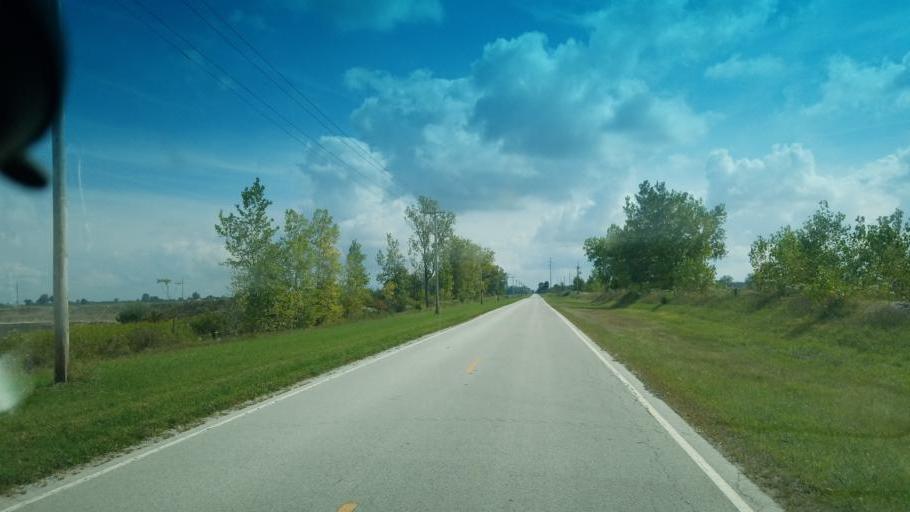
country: US
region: Ohio
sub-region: Wyandot County
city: Carey
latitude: 40.9635
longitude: -83.3528
